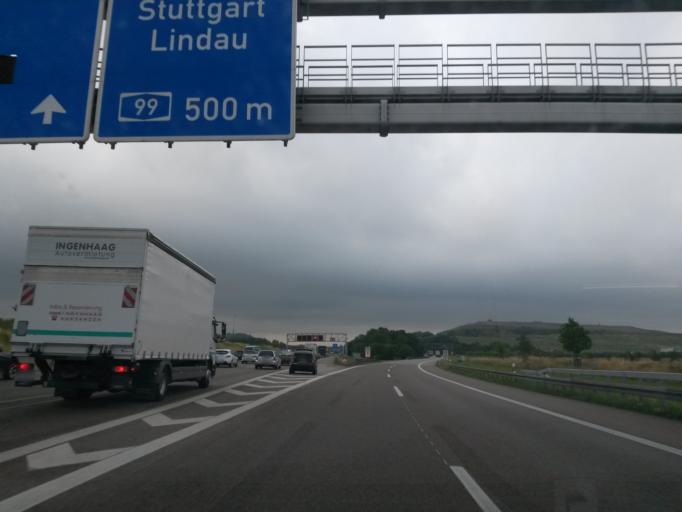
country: DE
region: Bavaria
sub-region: Upper Bavaria
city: Garching bei Munchen
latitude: 48.2313
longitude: 11.6341
